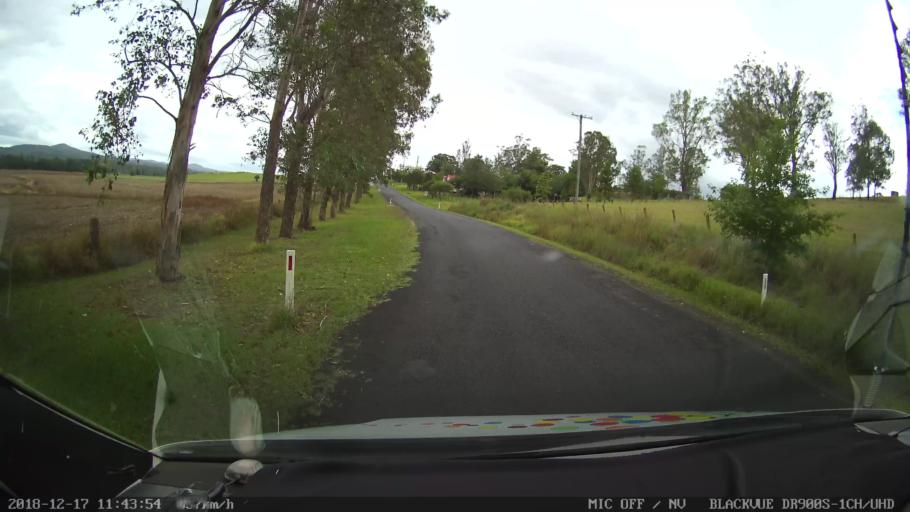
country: AU
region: New South Wales
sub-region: Kyogle
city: Kyogle
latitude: -28.6564
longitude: 152.5945
